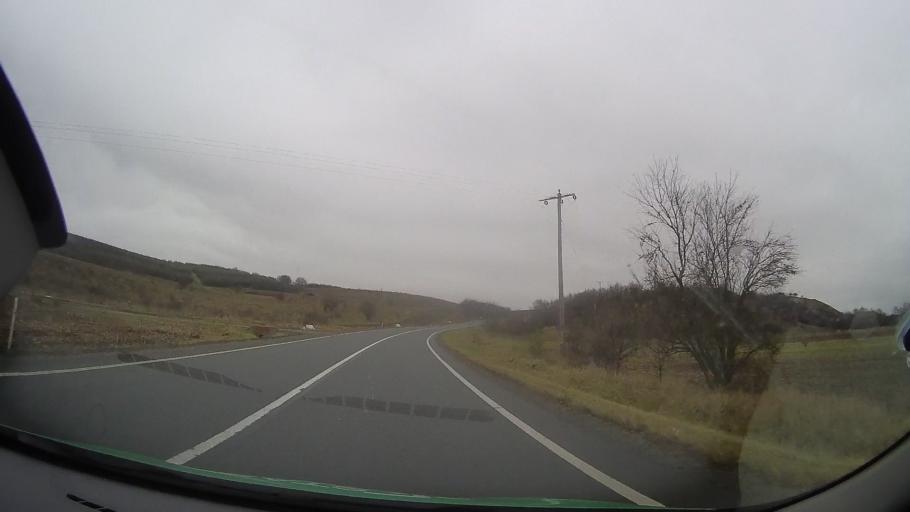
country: RO
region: Mures
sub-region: Comuna Breaza
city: Breaza
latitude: 46.7871
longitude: 24.6472
